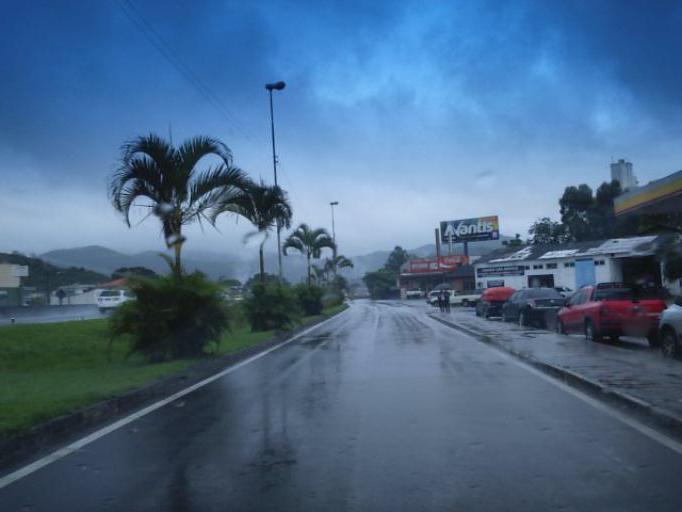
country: BR
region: Santa Catarina
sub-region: Itapema
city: Itapema
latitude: -27.1044
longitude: -48.6159
